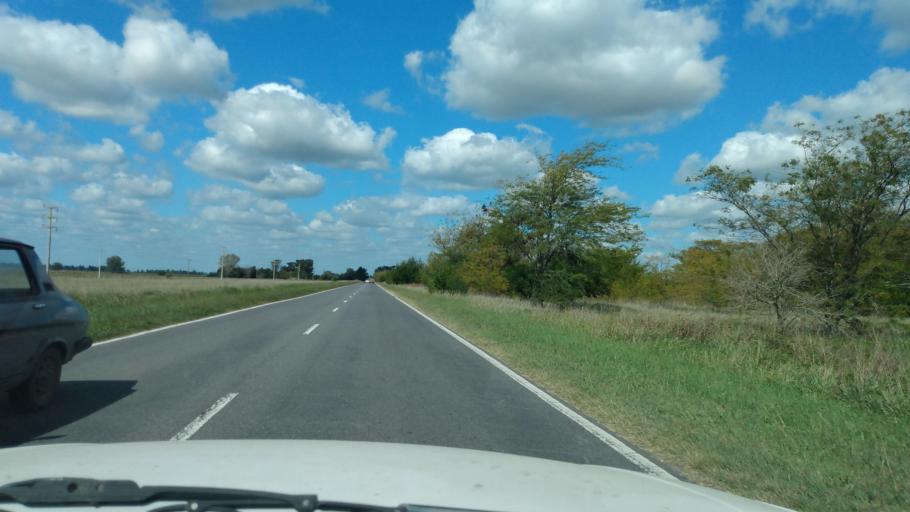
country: AR
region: Buenos Aires
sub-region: Partido de Navarro
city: Navarro
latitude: -34.9263
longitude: -59.3258
